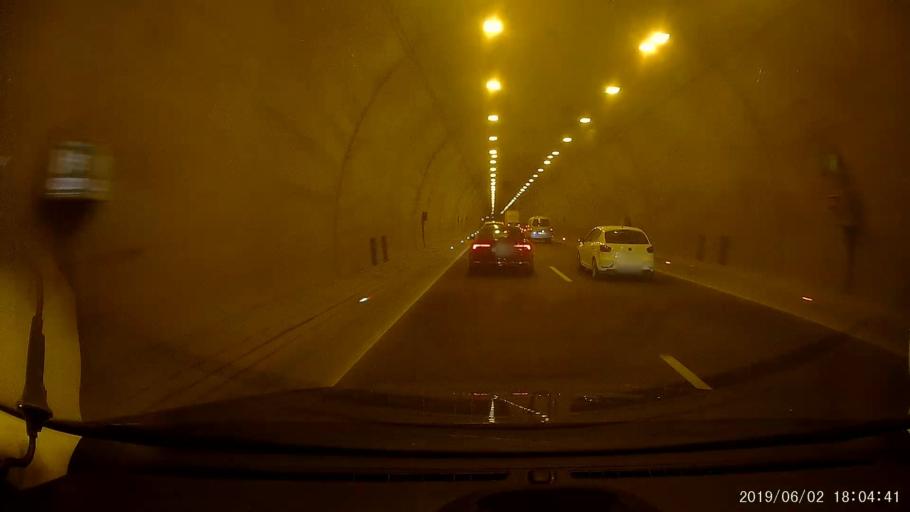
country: TR
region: Ordu
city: Unieh
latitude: 41.1192
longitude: 37.2335
